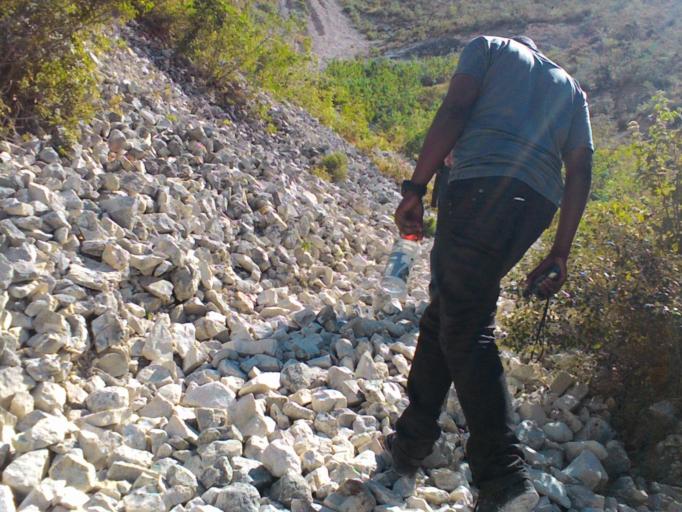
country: HT
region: Ouest
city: Croix des Bouquets
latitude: 18.6802
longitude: -72.2310
